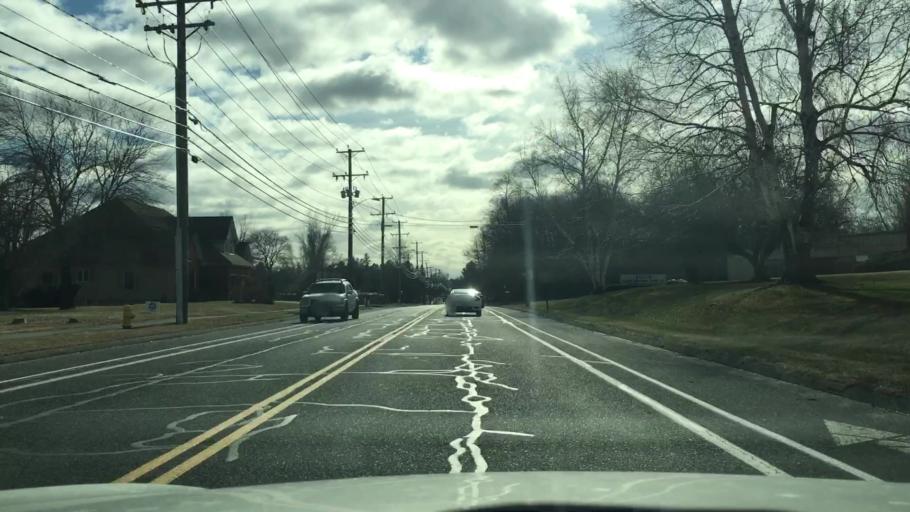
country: US
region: Massachusetts
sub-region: Hampden County
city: Agawam
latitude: 42.0525
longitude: -72.6341
